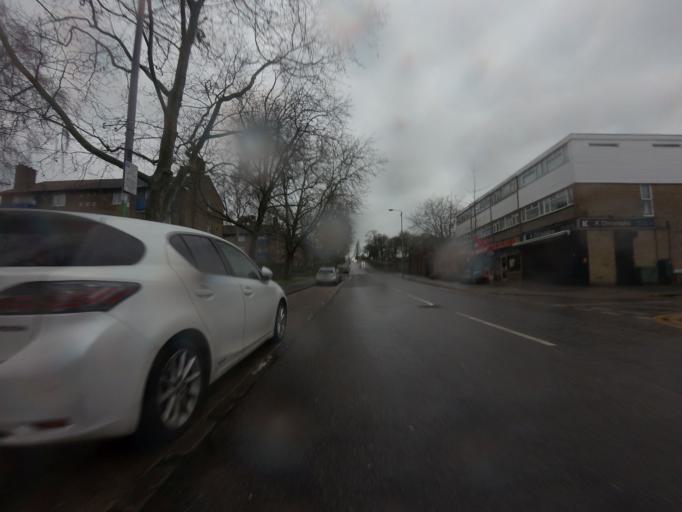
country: GB
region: England
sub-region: Greater London
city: Walthamstow
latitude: 51.6205
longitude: -0.0171
